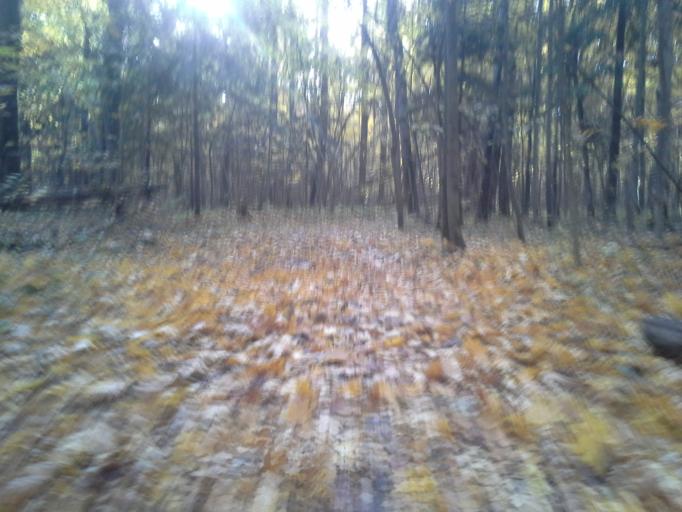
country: RU
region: Moskovskaya
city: Kommunarka
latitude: 55.5632
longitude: 37.5237
